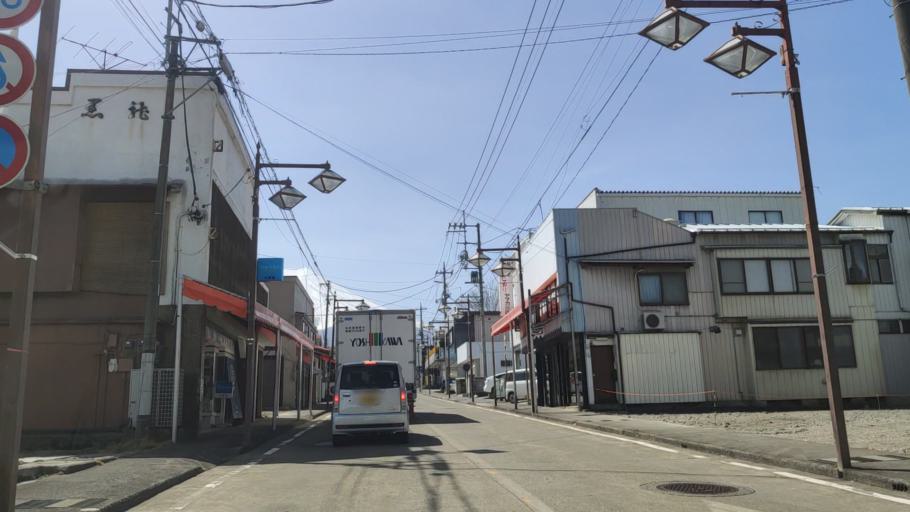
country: JP
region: Yamanashi
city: Fujikawaguchiko
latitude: 35.4846
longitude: 138.7990
